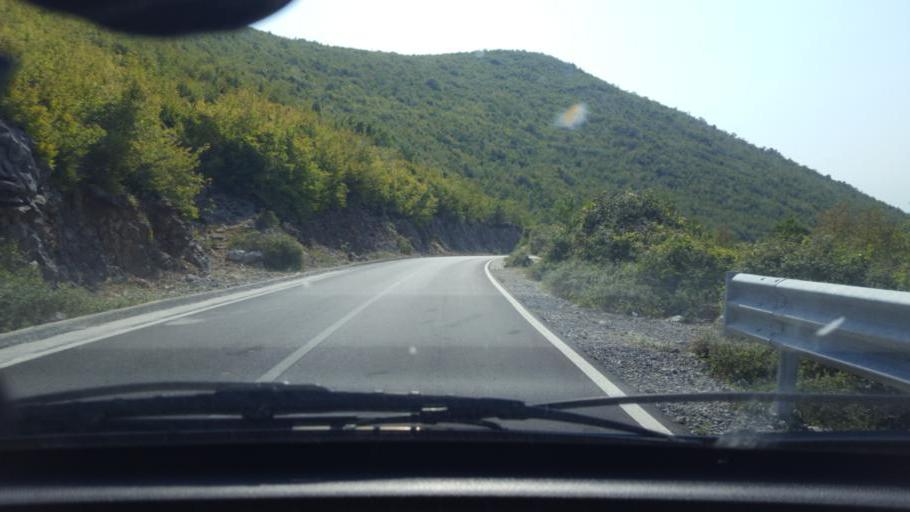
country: AL
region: Shkoder
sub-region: Rrethi i Malesia e Madhe
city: Kastrat
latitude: 42.3745
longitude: 19.4842
